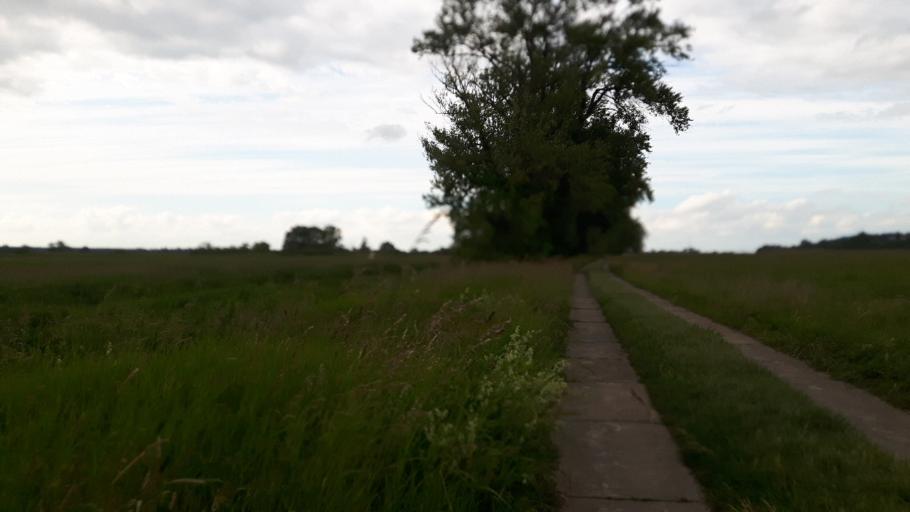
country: PL
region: West Pomeranian Voivodeship
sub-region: Powiat gryfinski
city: Widuchowa
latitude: 53.1209
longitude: 14.3779
